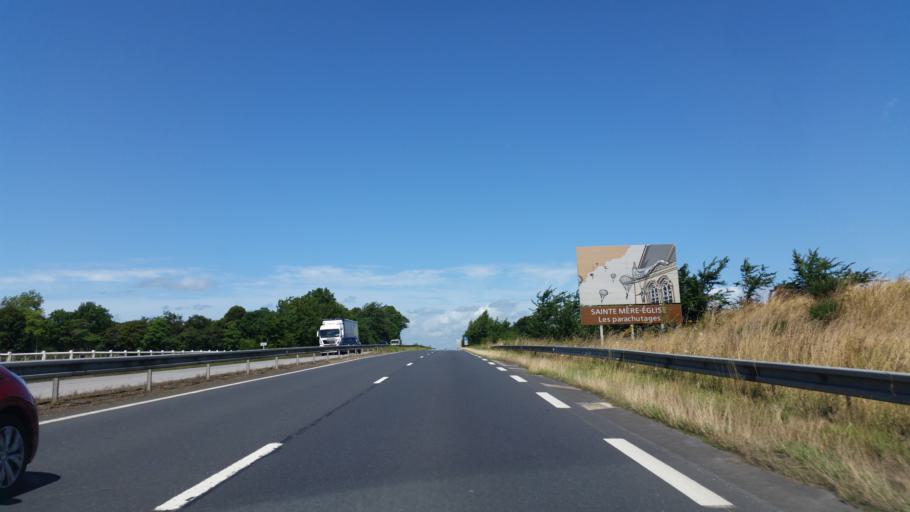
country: FR
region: Lower Normandy
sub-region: Departement de la Manche
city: Carentan
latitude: 49.3497
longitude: -1.2762
